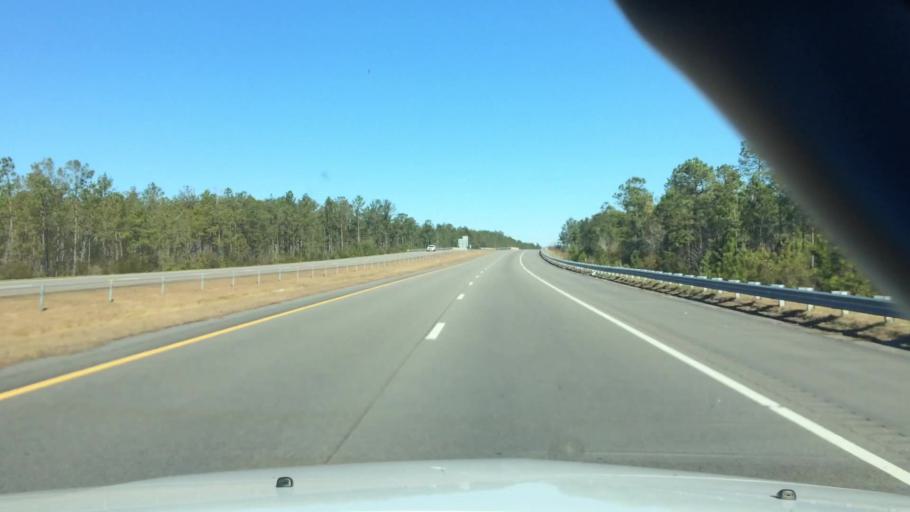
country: US
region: North Carolina
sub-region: Brunswick County
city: Leland
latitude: 34.2154
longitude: -78.0767
